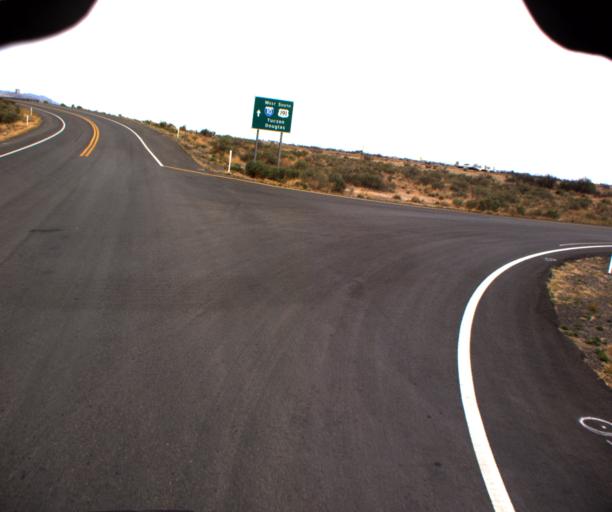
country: US
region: Arizona
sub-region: Cochise County
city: Willcox
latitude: 32.2208
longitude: -109.8759
